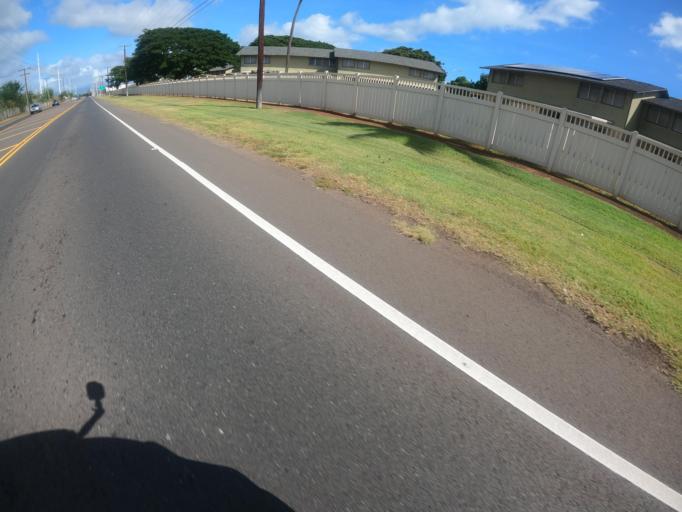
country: US
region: Hawaii
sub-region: Honolulu County
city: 'Ewa Villages
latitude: 21.3284
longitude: -158.0570
